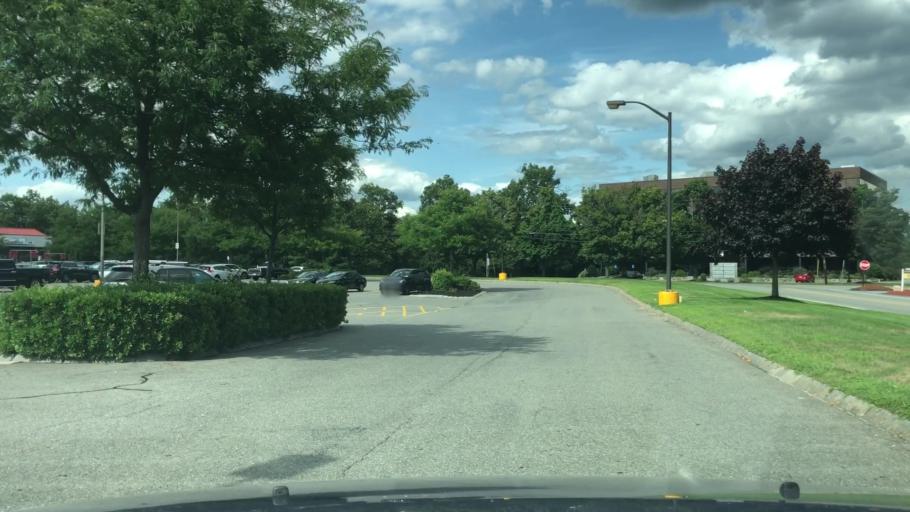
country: US
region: Massachusetts
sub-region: Middlesex County
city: Tewksbury
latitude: 42.6304
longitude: -71.2715
